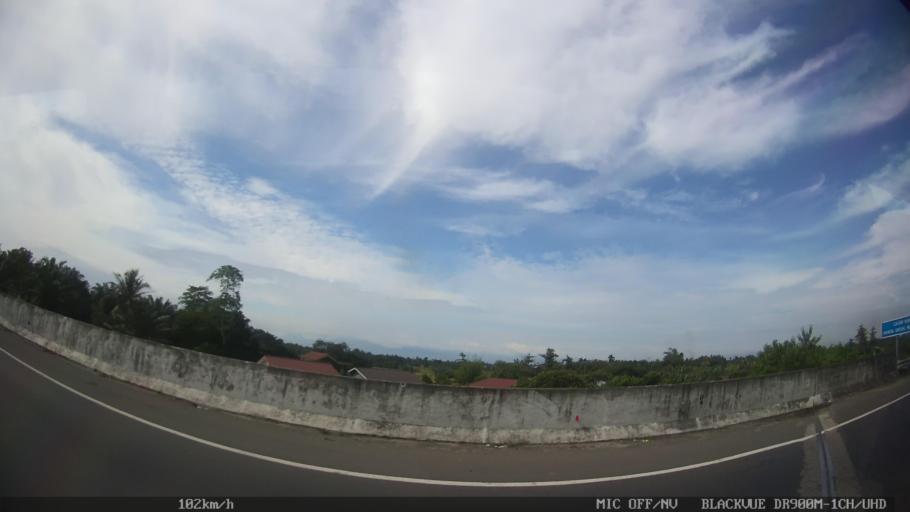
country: ID
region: North Sumatra
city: Sunggal
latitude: 3.6392
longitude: 98.5736
